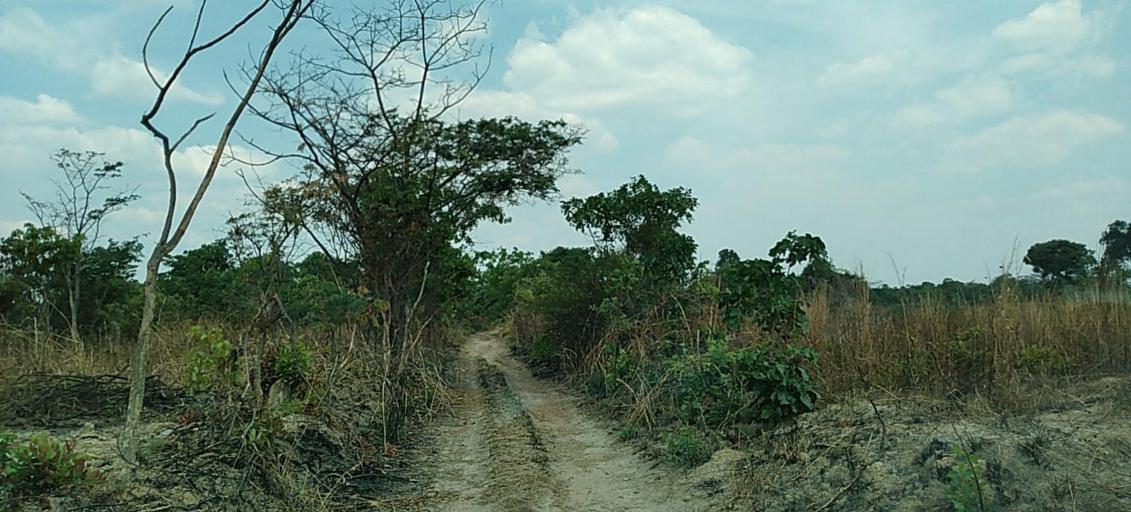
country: ZM
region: Copperbelt
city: Chililabombwe
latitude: -12.3404
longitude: 27.7794
